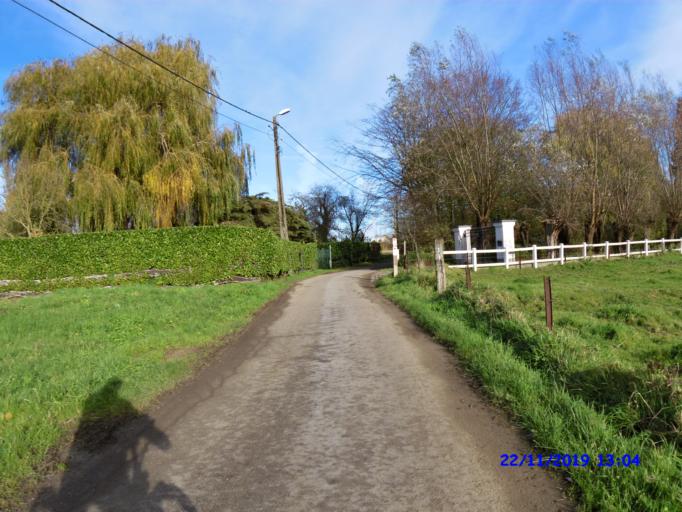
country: BE
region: Flanders
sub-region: Provincie Vlaams-Brabant
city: Londerzeel
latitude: 50.9886
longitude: 4.3058
